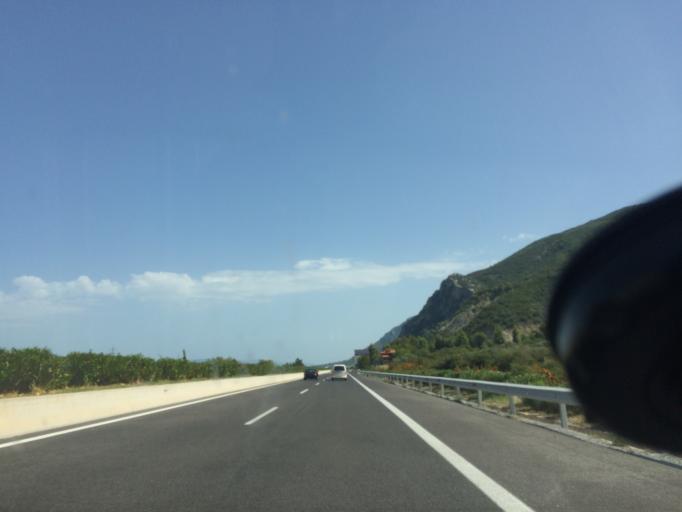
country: GR
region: Central Greece
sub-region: Nomos Fthiotidos
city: Kainouryion
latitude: 38.7792
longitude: 22.7273
